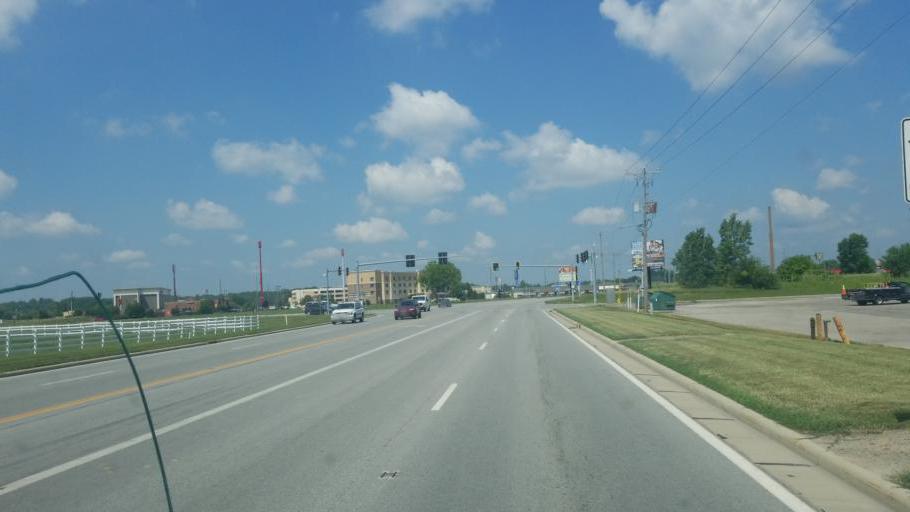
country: US
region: Ohio
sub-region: Allen County
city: Lima
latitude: 40.7274
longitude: -84.0677
